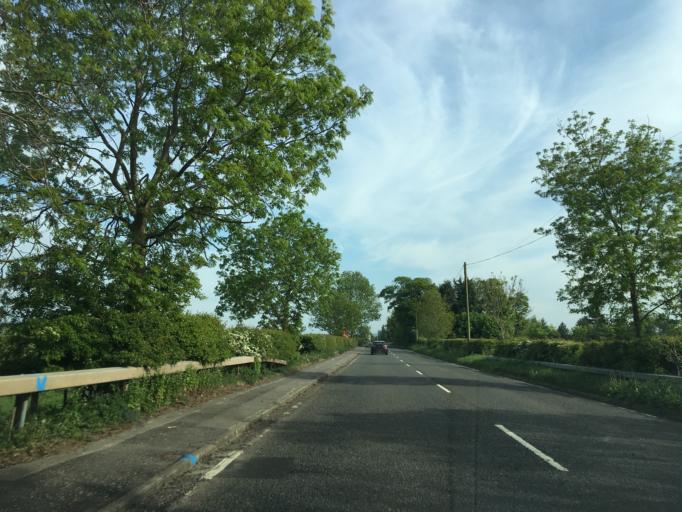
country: GB
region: Scotland
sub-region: Midlothian
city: Loanhead
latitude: 55.8667
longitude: -3.1876
